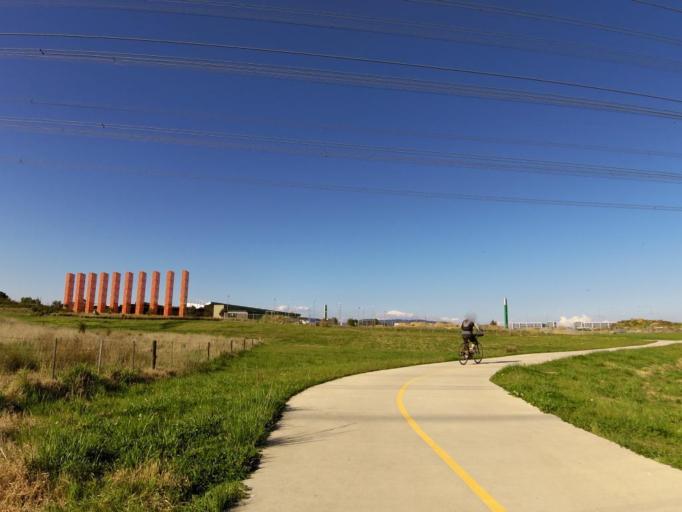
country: AU
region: Victoria
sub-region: Monash
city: Mulgrave
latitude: -37.9141
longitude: 145.2118
